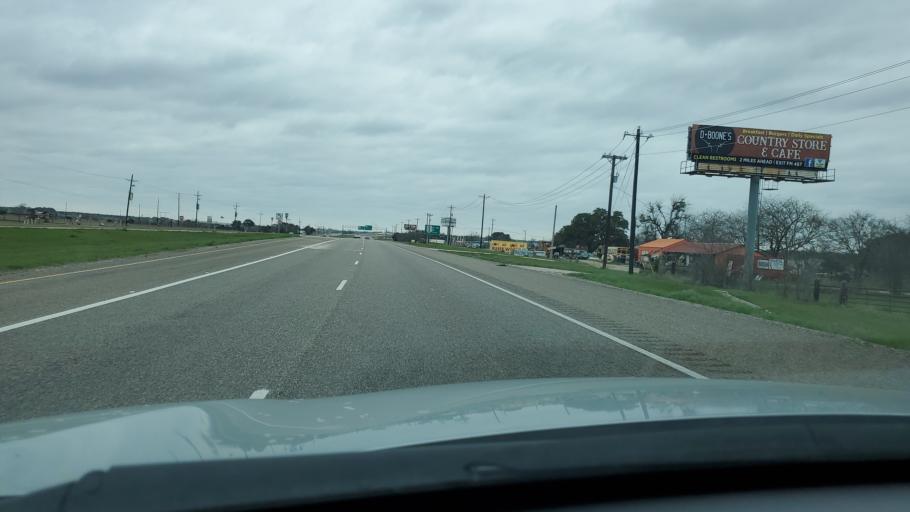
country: US
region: Texas
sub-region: Williamson County
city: Florence
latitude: 30.8131
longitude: -97.7738
